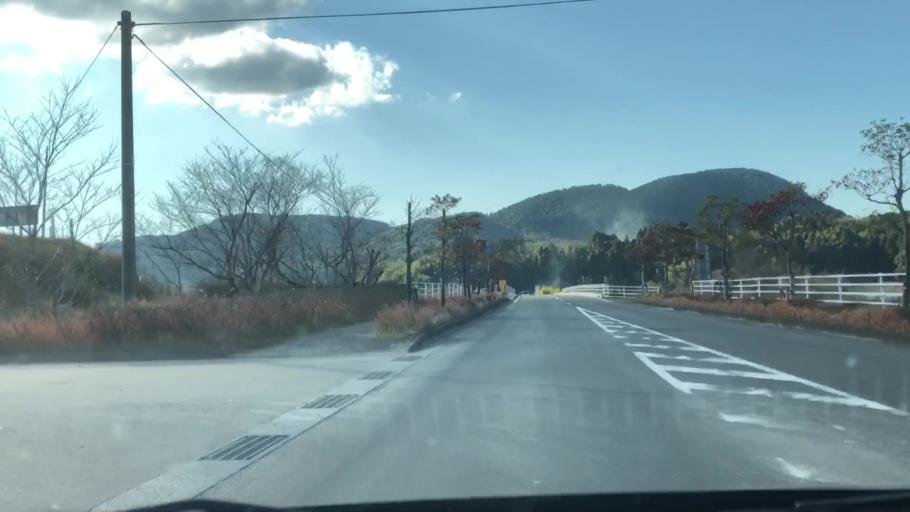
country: JP
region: Kagoshima
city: Satsumasendai
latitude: 31.8653
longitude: 130.3279
